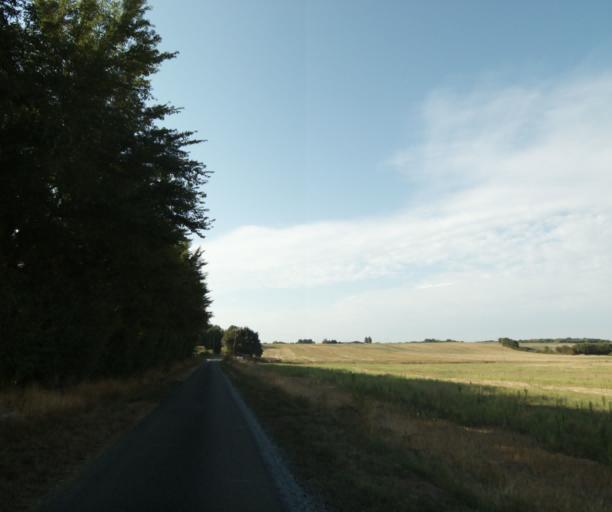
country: FR
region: Poitou-Charentes
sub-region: Departement de la Charente-Maritime
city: Cabariot
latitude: 45.9751
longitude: -0.8271
